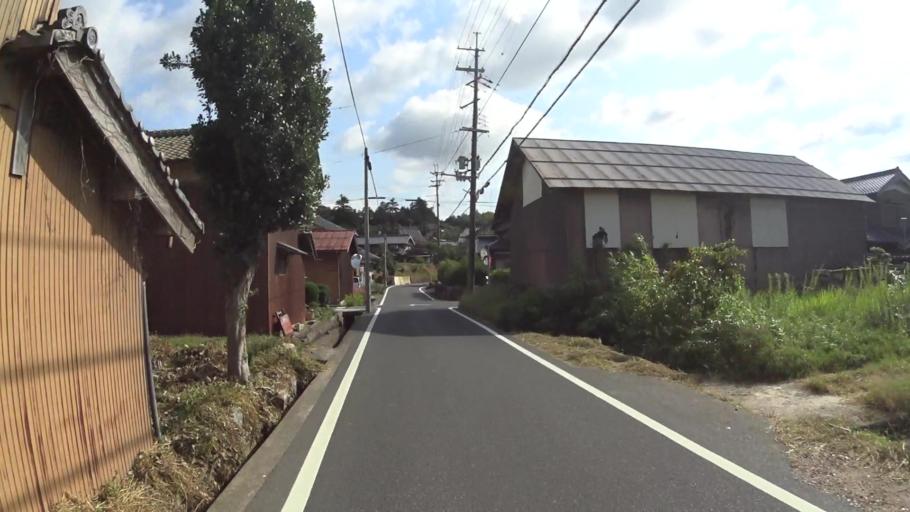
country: JP
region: Kyoto
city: Miyazu
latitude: 35.6190
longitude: 135.0834
